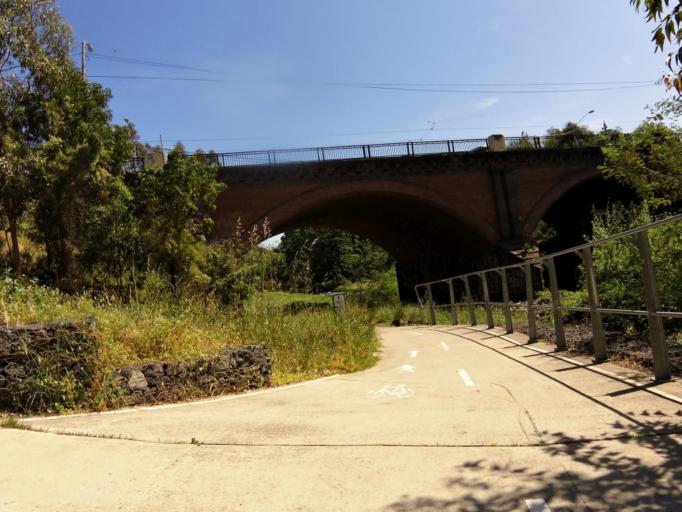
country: AU
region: Victoria
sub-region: Yarra
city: Clifton Hill
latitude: -37.7850
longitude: 144.9958
